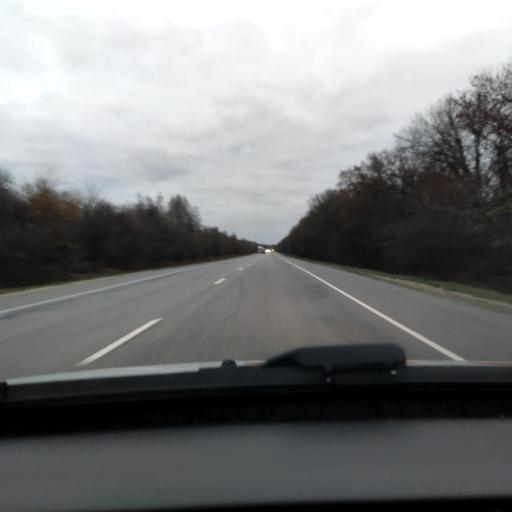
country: RU
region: Lipetsk
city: Khlevnoye
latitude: 52.3579
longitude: 39.1984
